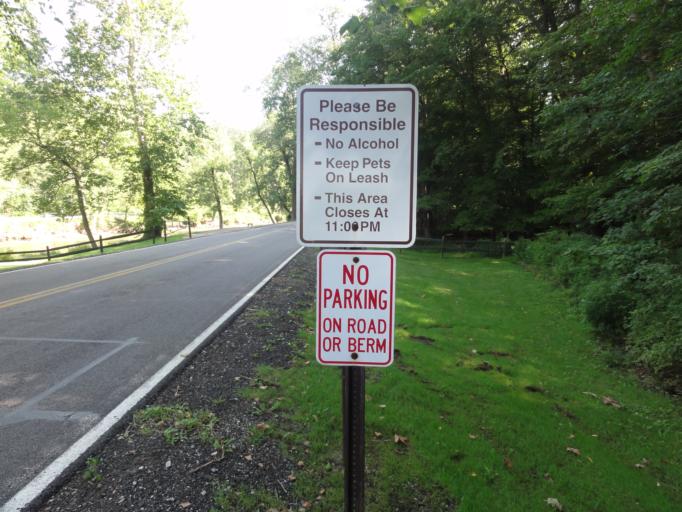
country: US
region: Ohio
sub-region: Cuyahoga County
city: Walton Hills
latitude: 41.3733
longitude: -81.5793
